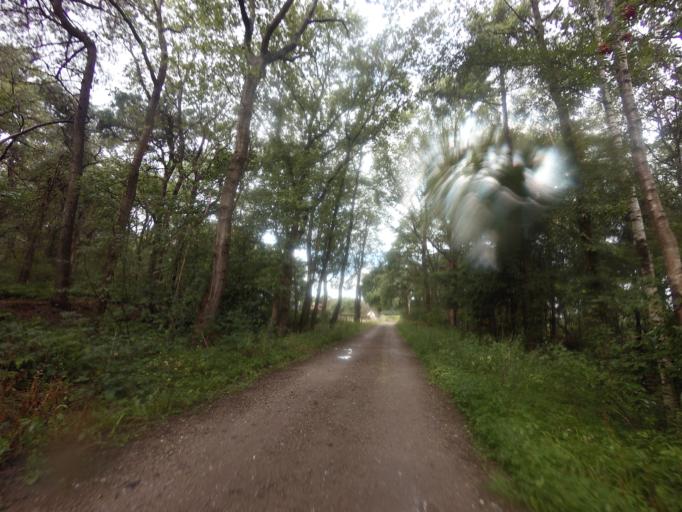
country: NL
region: Overijssel
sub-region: Gemeente Staphorst
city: Staphorst
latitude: 52.6160
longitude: 6.3207
